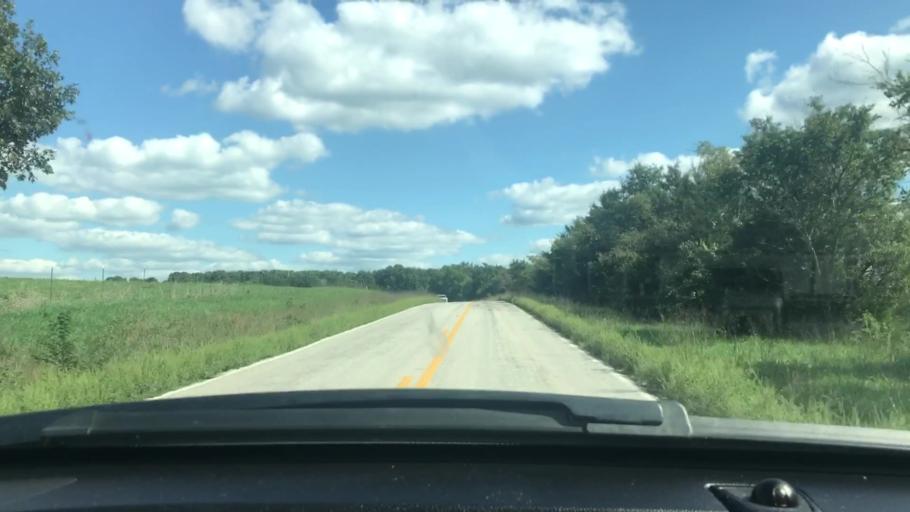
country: US
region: Missouri
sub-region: Wright County
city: Hartville
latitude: 37.3796
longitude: -92.4358
